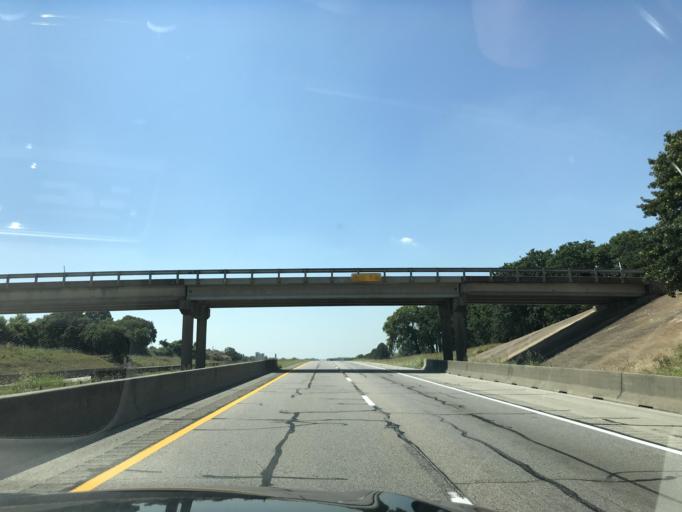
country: US
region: Texas
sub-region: Johnson County
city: Alvarado
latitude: 32.3803
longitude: -97.2056
